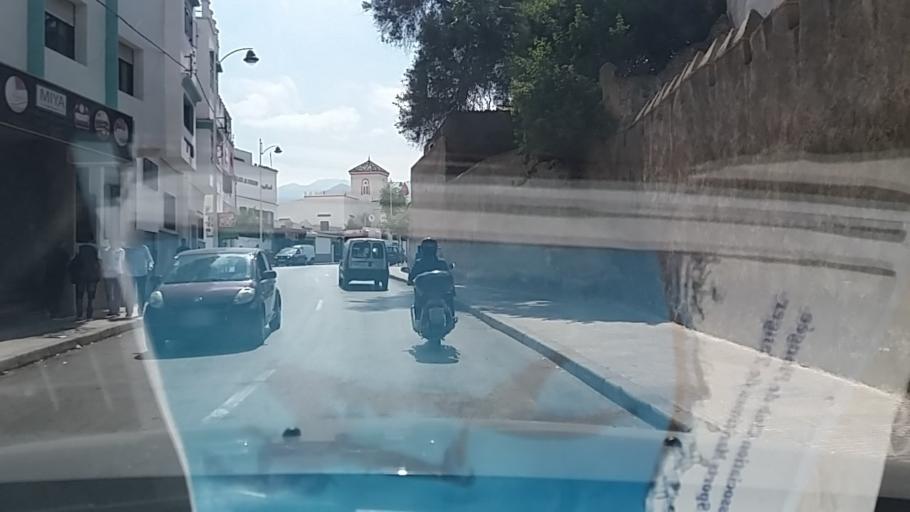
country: MA
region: Tanger-Tetouan
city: Tetouan
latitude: 35.5725
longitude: -5.3632
